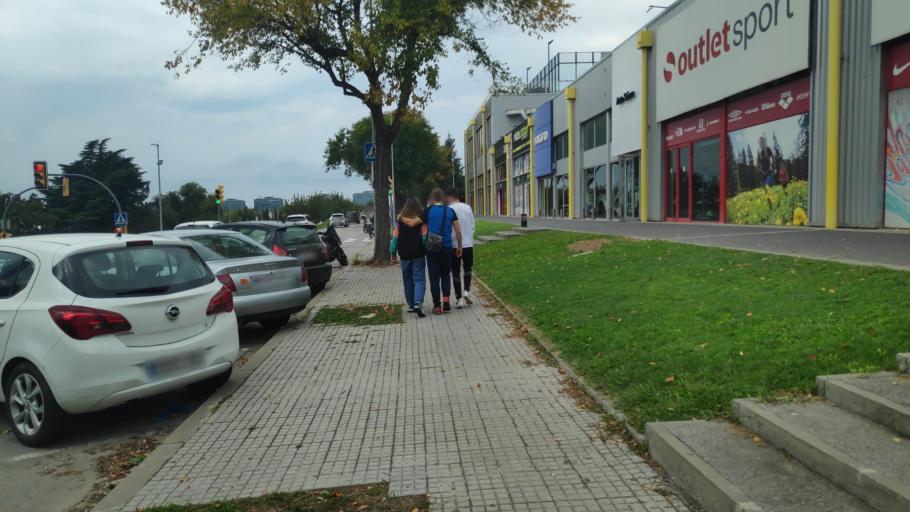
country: ES
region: Catalonia
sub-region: Provincia de Barcelona
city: Sant Cugat del Valles
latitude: 41.4800
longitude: 2.0598
